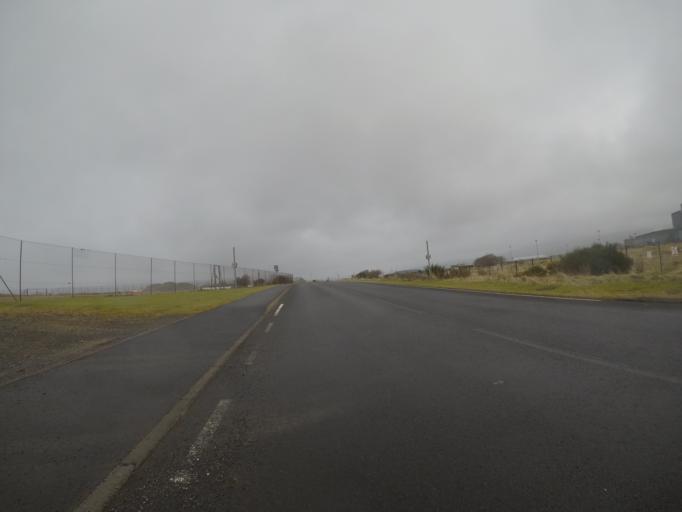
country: GB
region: Scotland
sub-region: North Ayrshire
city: Millport
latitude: 55.7210
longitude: -4.8999
